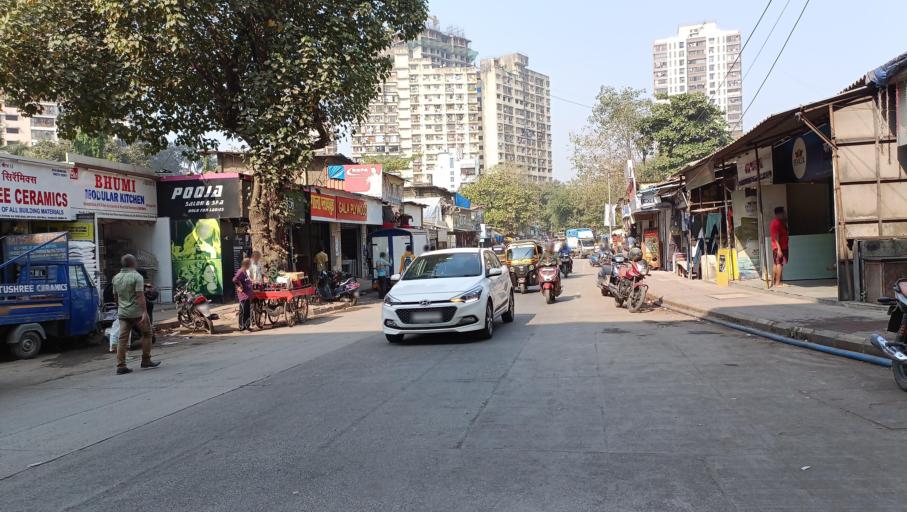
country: IN
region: Maharashtra
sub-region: Mumbai Suburban
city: Borivli
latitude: 19.2504
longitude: 72.8663
